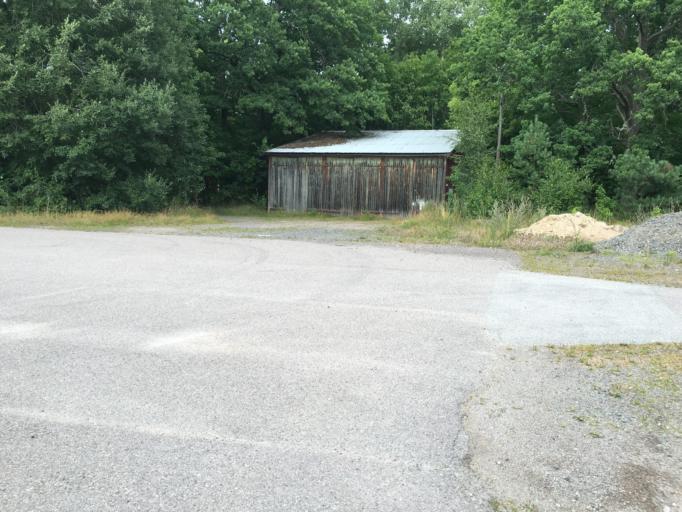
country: SE
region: Kalmar
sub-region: Nybro Kommun
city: Nybro
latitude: 56.9427
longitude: 15.9162
